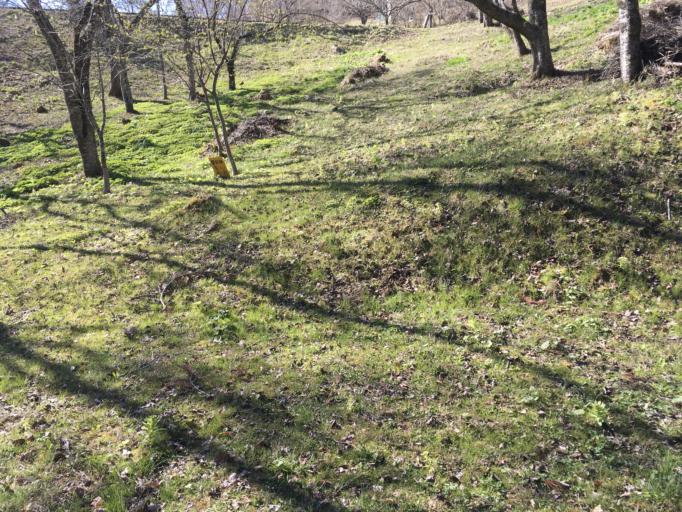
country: JP
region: Iwate
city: Ichinoseki
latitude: 38.9397
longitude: 141.2305
